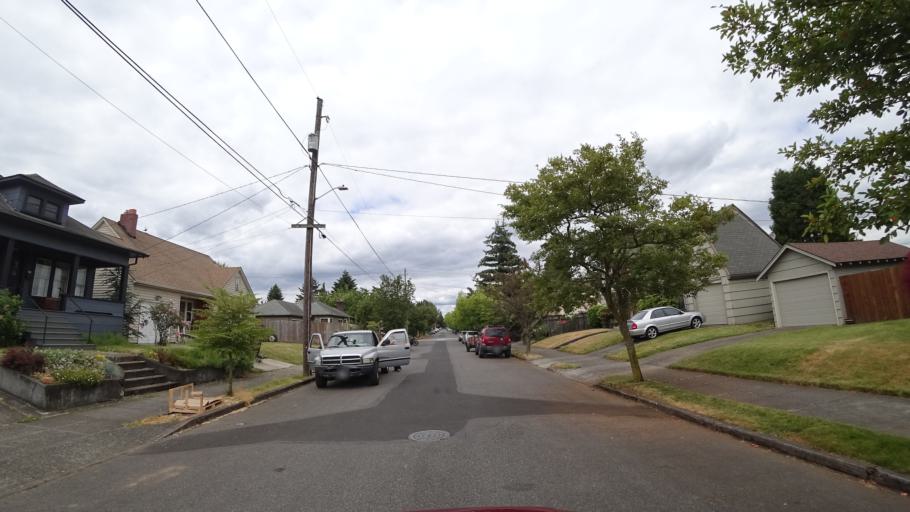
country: US
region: Oregon
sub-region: Multnomah County
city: Portland
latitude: 45.5758
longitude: -122.6719
